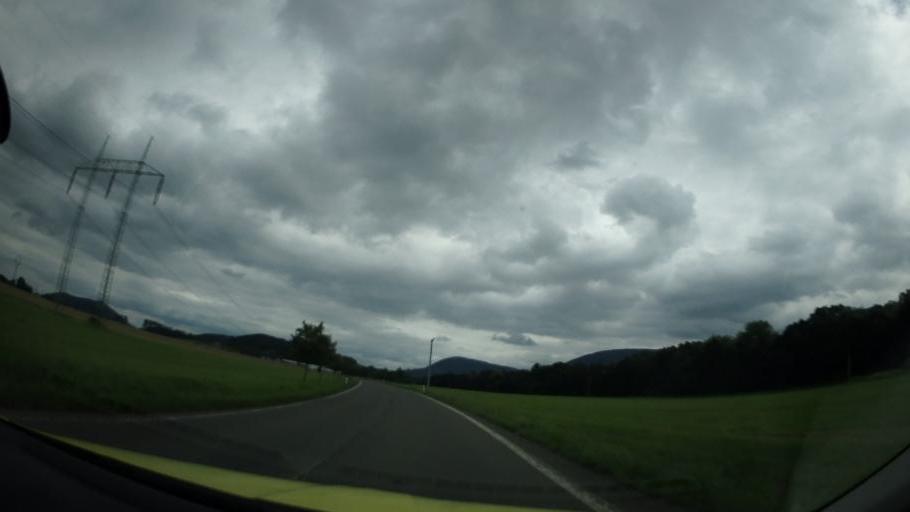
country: CZ
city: Morkov
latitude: 49.5436
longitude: 18.0771
